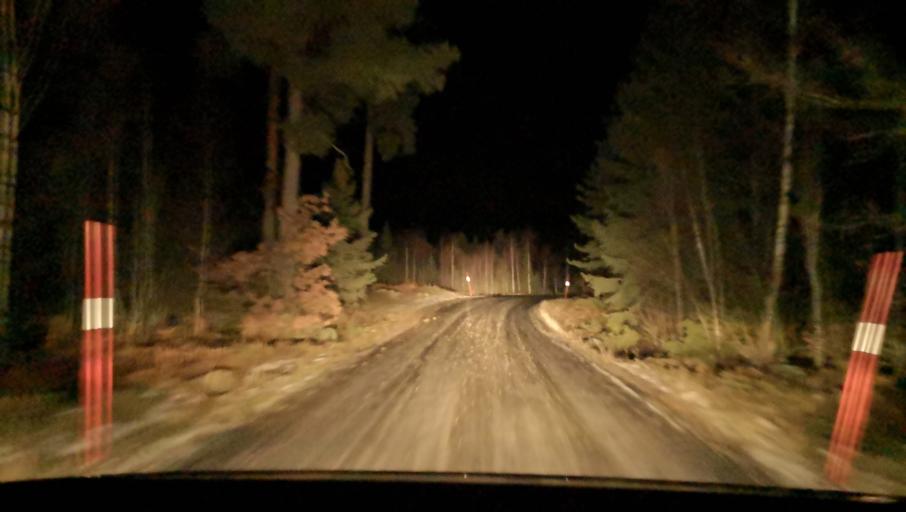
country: SE
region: Vaestmanland
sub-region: Vasteras
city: Tillberga
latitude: 59.6811
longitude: 16.6837
